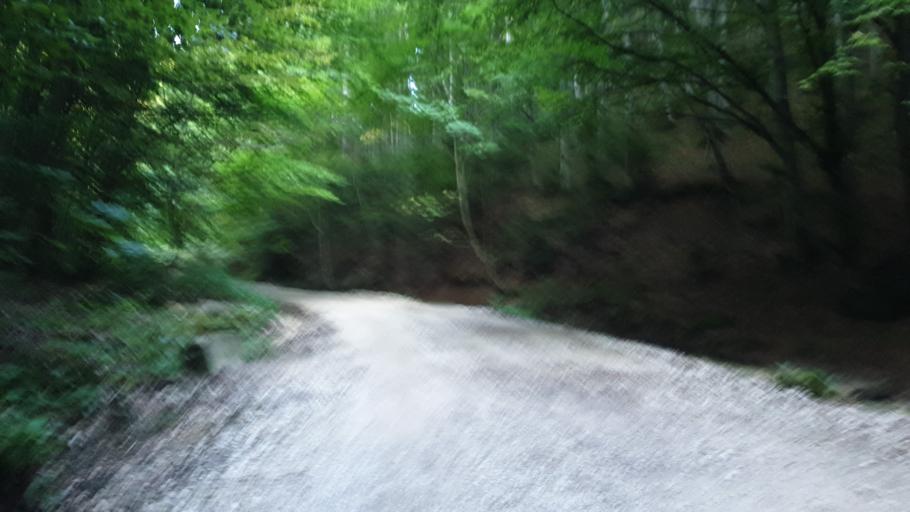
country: RO
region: Brasov
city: Brasov
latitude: 45.6144
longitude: 25.5610
